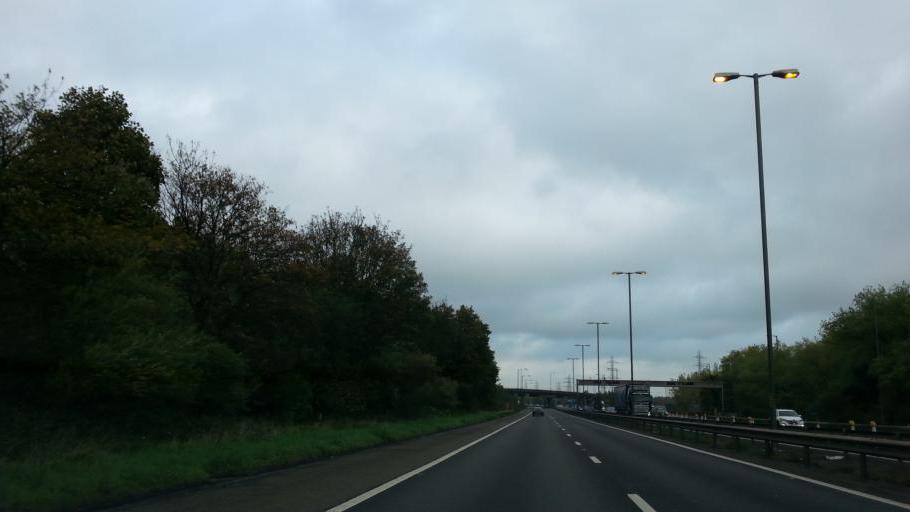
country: GB
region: England
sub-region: Sandwell
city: West Bromwich
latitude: 52.5384
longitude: -1.9691
